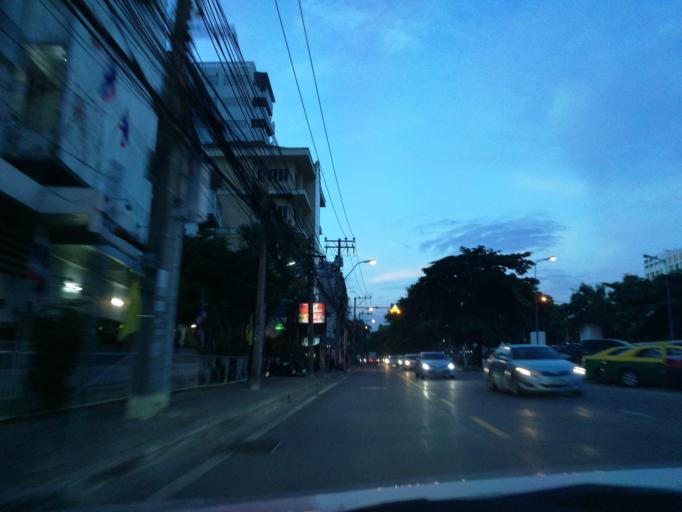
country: TH
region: Bangkok
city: Dusit
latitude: 13.7776
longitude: 100.5292
